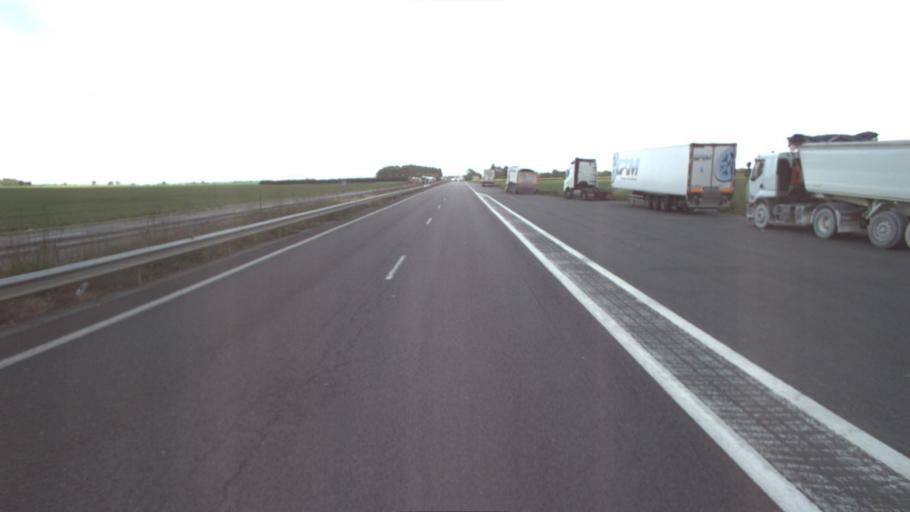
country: FR
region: Ile-de-France
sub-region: Departement de Seine-et-Marne
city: Fontenay-Tresigny
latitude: 48.6927
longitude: 2.9134
